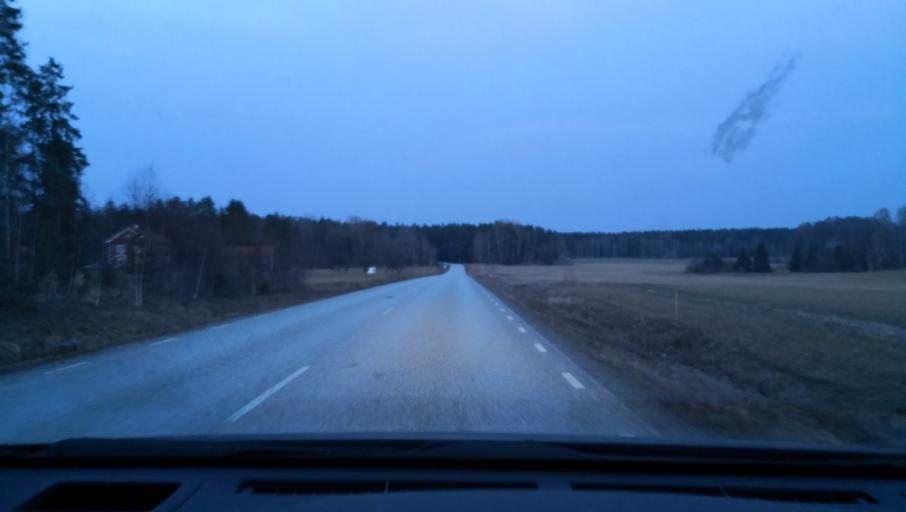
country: SE
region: OErebro
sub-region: Lindesbergs Kommun
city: Lindesberg
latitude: 59.5939
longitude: 15.3004
